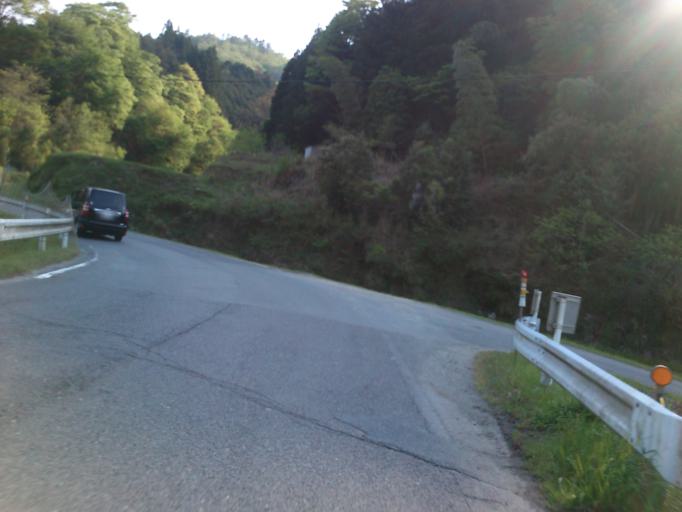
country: JP
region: Kyoto
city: Fukuchiyama
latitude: 35.2611
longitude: 135.0696
